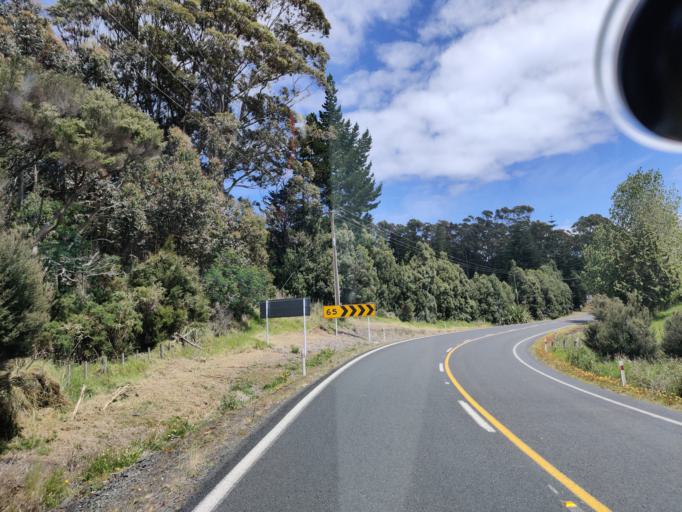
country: NZ
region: Northland
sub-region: Far North District
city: Kaitaia
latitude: -35.0047
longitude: 173.1935
